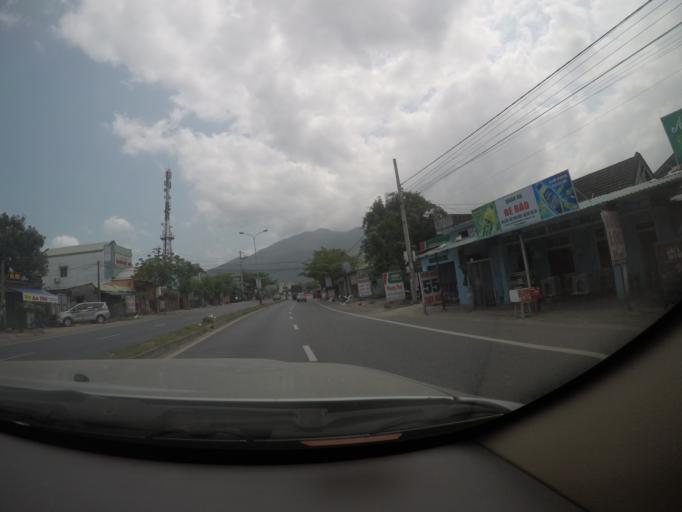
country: VN
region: Da Nang
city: Lien Chieu
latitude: 16.2336
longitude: 108.0831
